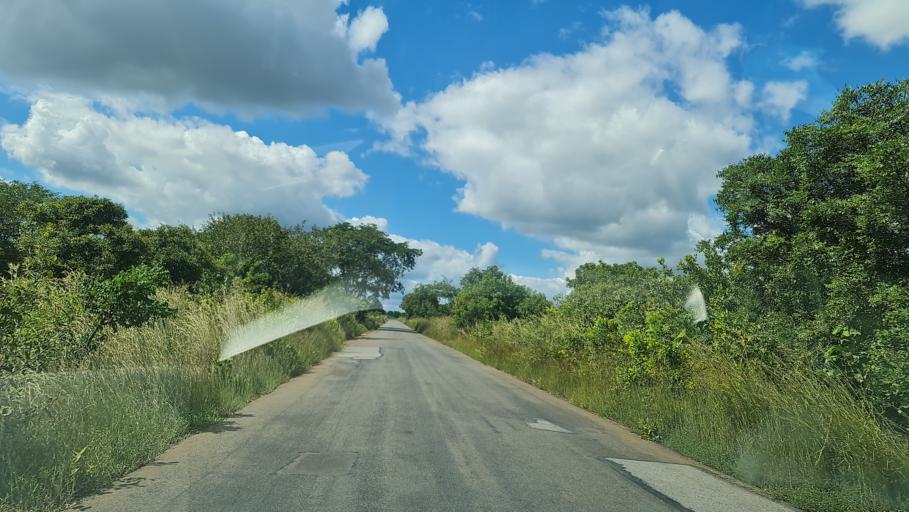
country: MZ
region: Zambezia
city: Quelimane
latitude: -17.5084
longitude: 36.2373
